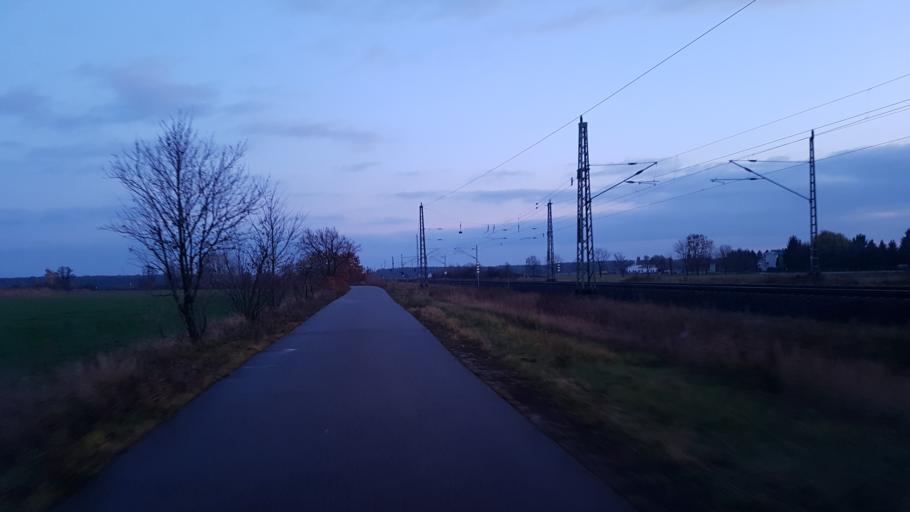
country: DE
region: Brandenburg
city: Falkenberg
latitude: 51.6253
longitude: 13.2035
